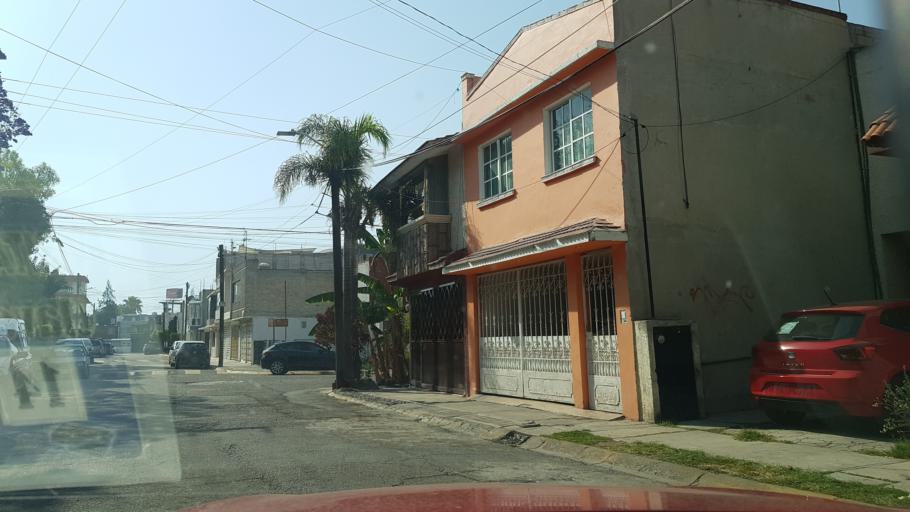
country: MX
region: Mexico
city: Santiago Teyahualco
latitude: 19.6534
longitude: -99.1164
